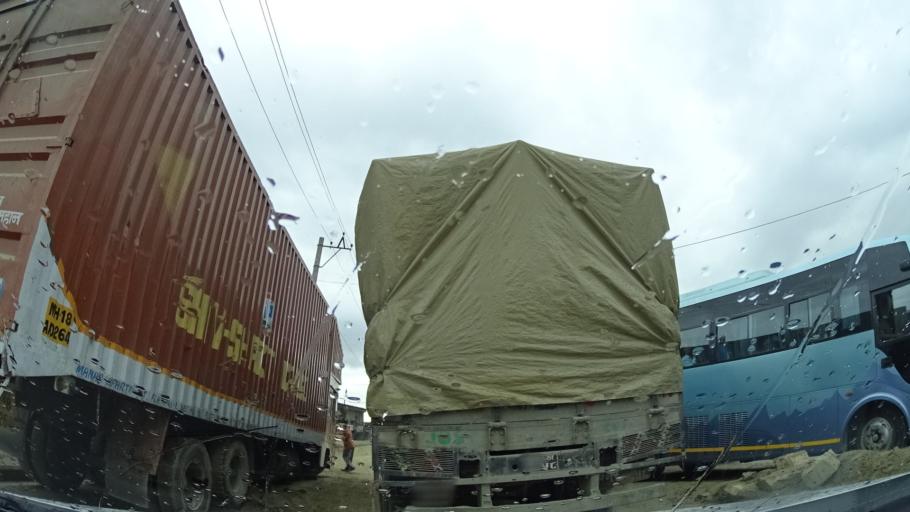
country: NP
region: Central Region
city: Kirtipur
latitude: 27.6991
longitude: 85.2090
